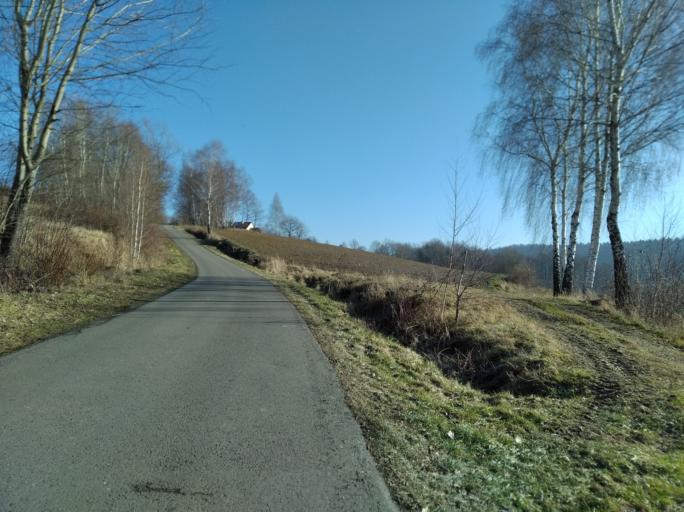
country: PL
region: Subcarpathian Voivodeship
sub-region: Powiat strzyzowski
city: Konieczkowa
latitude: 49.8584
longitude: 21.9384
